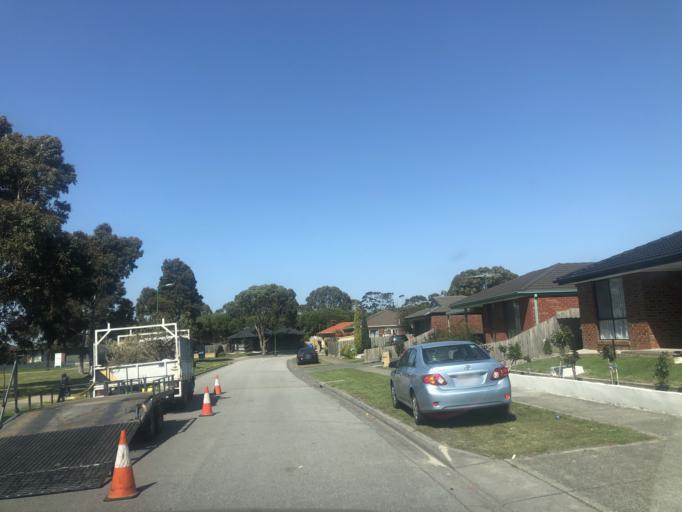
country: AU
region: Victoria
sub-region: Casey
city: Narre Warren South
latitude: -38.0511
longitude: 145.2779
